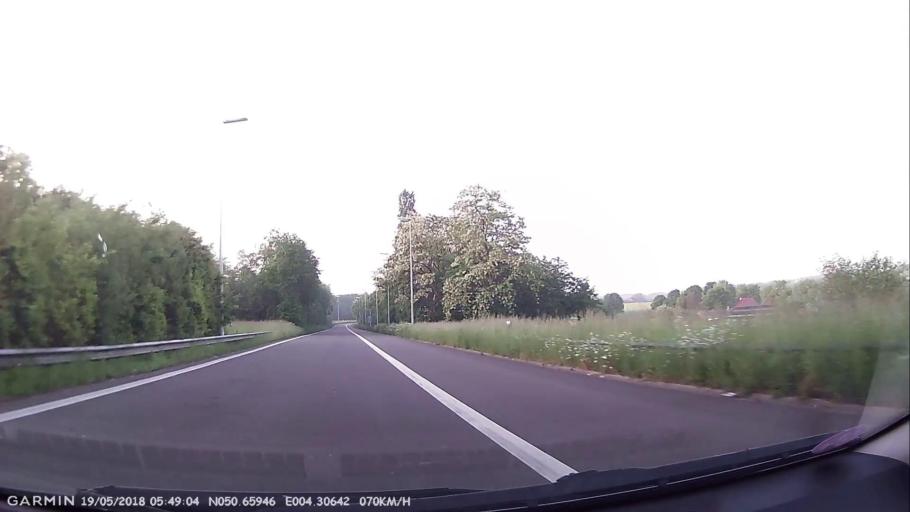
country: BE
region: Wallonia
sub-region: Province du Brabant Wallon
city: Braine-le-Chateau
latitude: 50.6593
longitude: 4.3065
